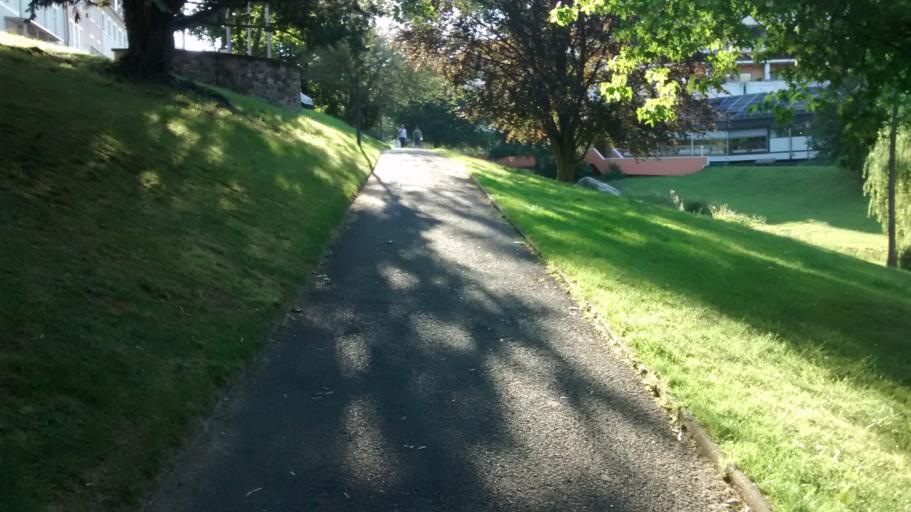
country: DE
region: Hesse
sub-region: Regierungsbezirk Darmstadt
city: Schlangenbad
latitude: 50.0931
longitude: 8.1024
